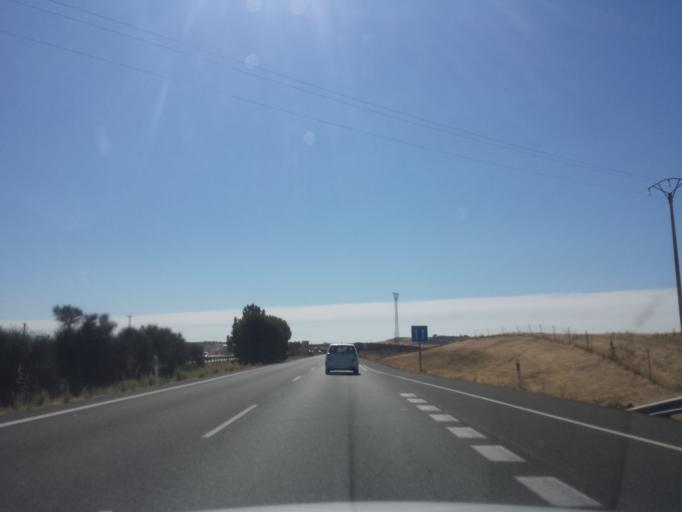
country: ES
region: Castille and Leon
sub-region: Provincia de Valladolid
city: Mota del Marques
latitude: 41.6277
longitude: -5.1790
